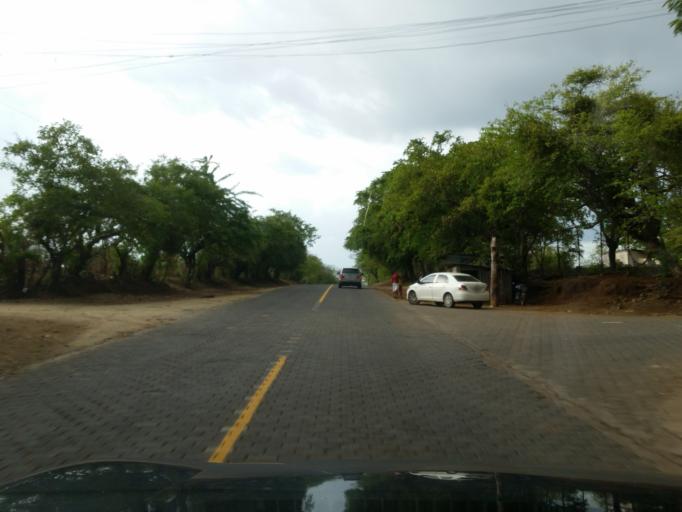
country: NI
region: Managua
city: Carlos Fonseca Amador
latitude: 11.9779
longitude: -86.5149
